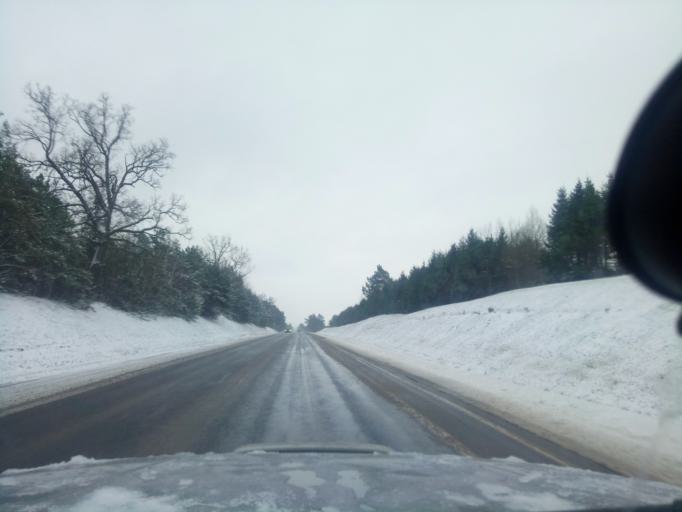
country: BY
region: Minsk
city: Nyasvizh
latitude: 53.2619
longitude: 26.6093
